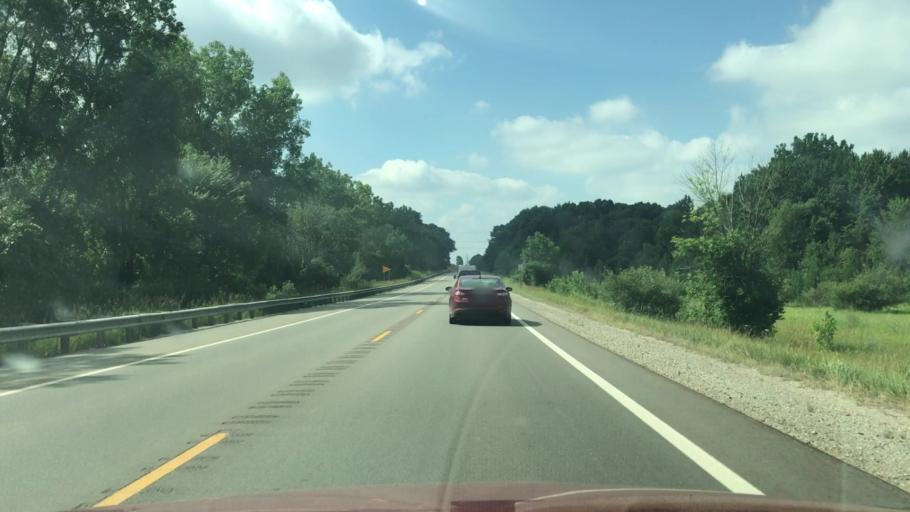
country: US
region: Michigan
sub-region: Kent County
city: Sparta
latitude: 43.1853
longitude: -85.7202
